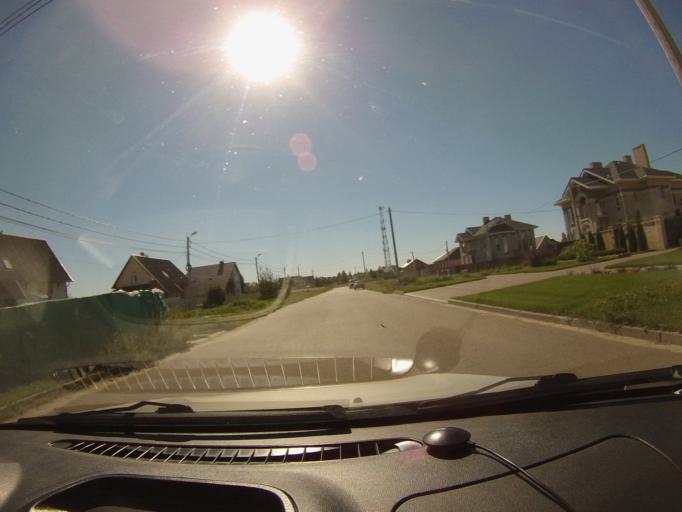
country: RU
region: Tambov
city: Tambov
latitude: 52.7671
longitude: 41.3791
